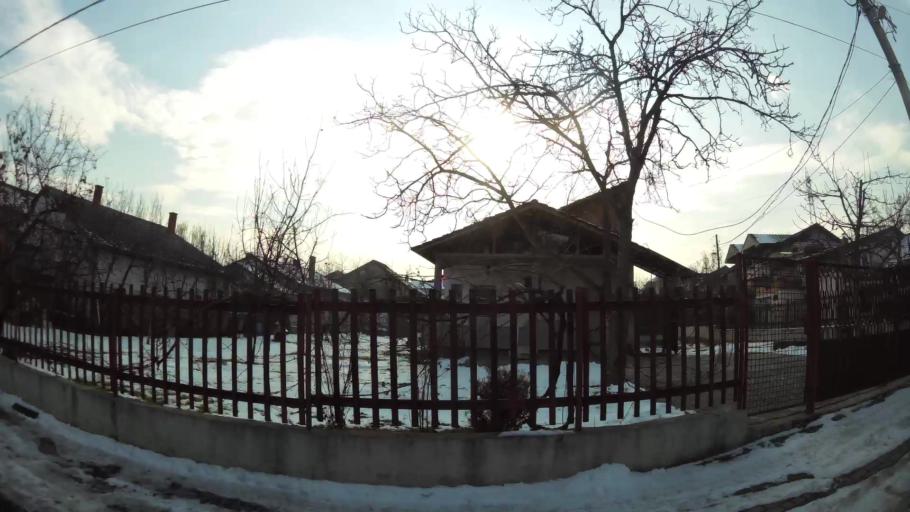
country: MK
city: Creshevo
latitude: 42.0120
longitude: 21.4977
